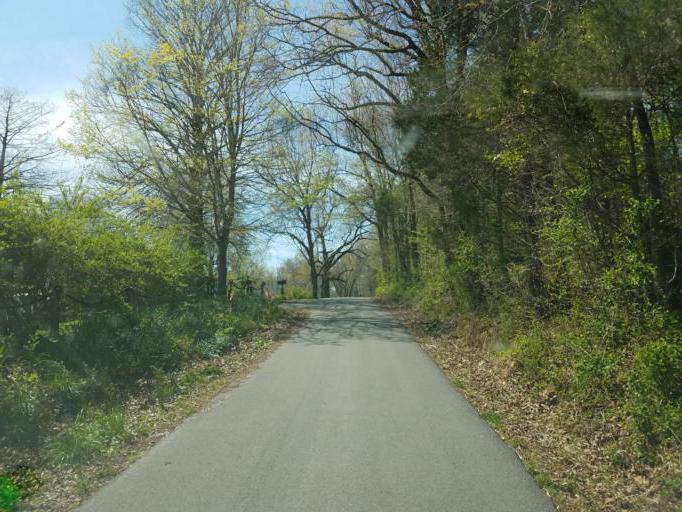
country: US
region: Kentucky
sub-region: Barren County
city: Cave City
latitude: 37.1913
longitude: -86.0479
